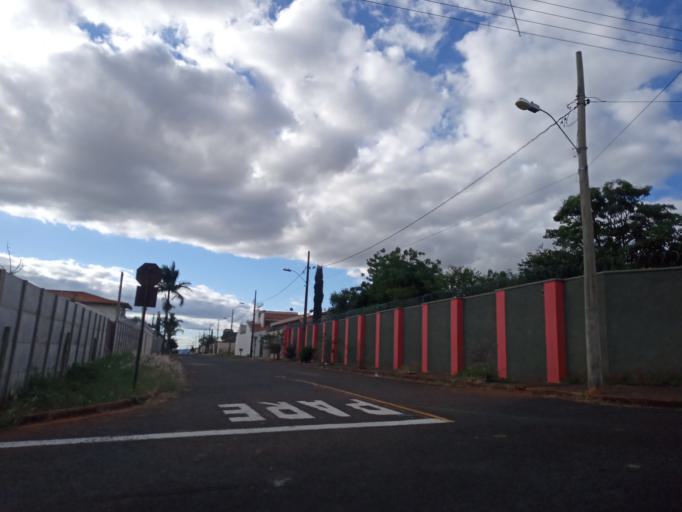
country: BR
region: Minas Gerais
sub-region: Ituiutaba
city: Ituiutaba
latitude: -18.9947
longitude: -49.4578
